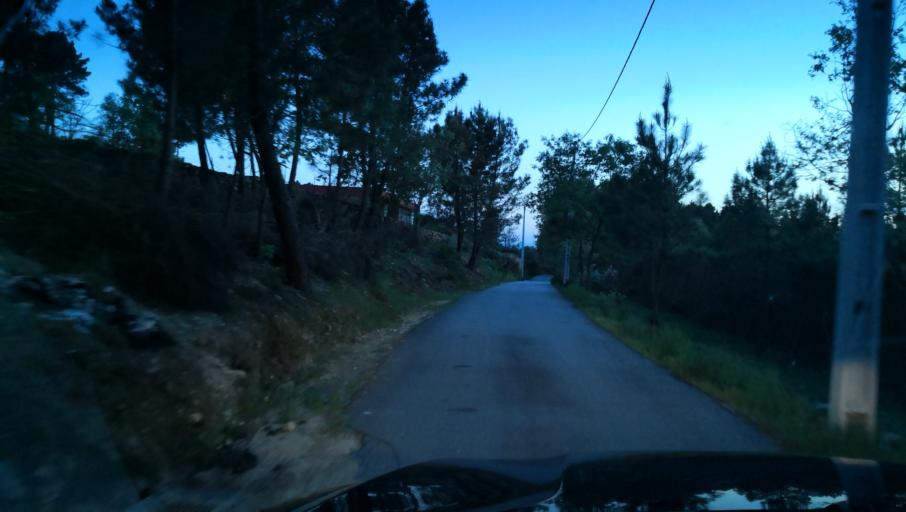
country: PT
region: Vila Real
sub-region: Vila Real
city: Vila Real
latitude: 41.3534
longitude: -7.6933
